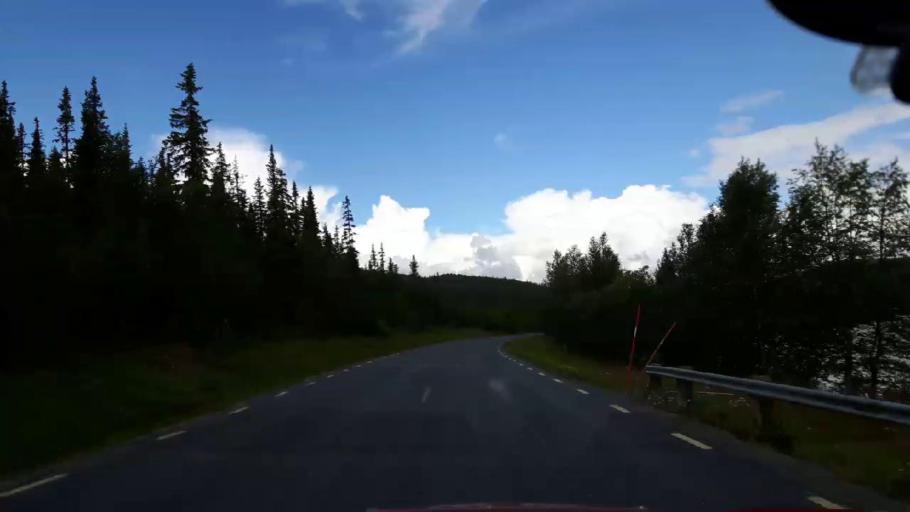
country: SE
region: Vaesterbotten
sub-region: Vilhelmina Kommun
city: Sjoberg
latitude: 65.0105
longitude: 15.1766
